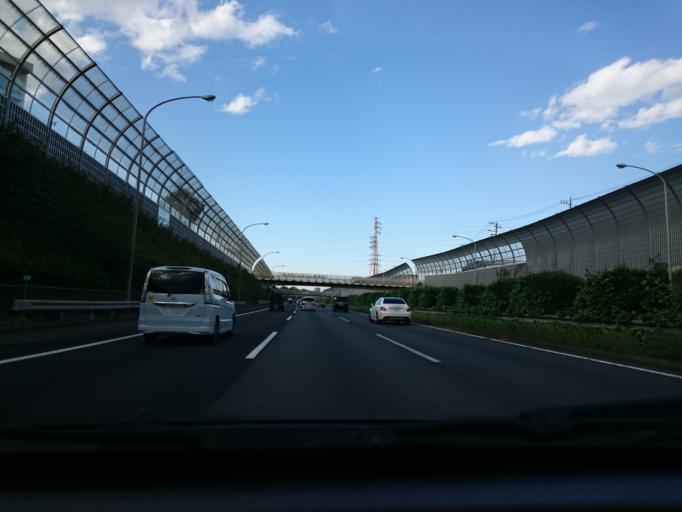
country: JP
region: Kanagawa
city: Minami-rinkan
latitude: 35.4558
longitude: 139.4282
